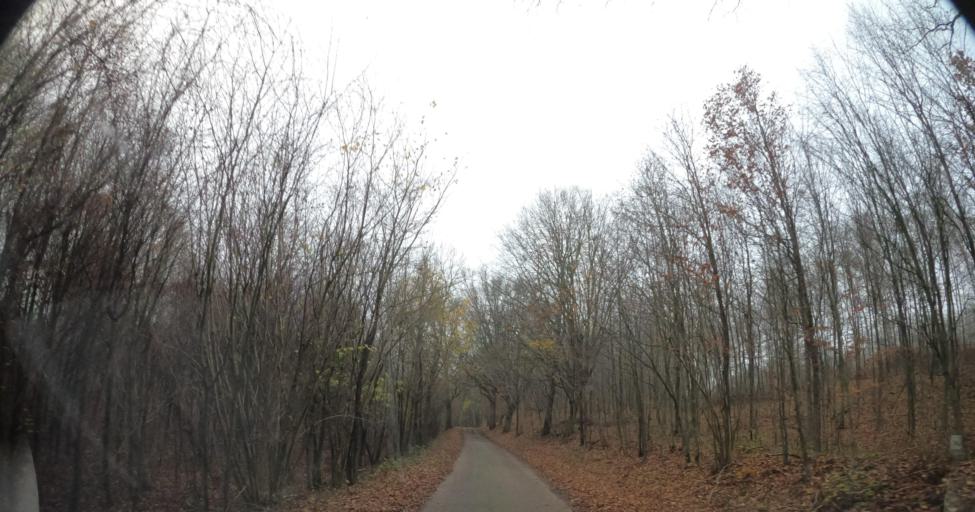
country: PL
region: West Pomeranian Voivodeship
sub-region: Powiat drawski
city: Drawsko Pomorskie
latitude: 53.5820
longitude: 15.8054
